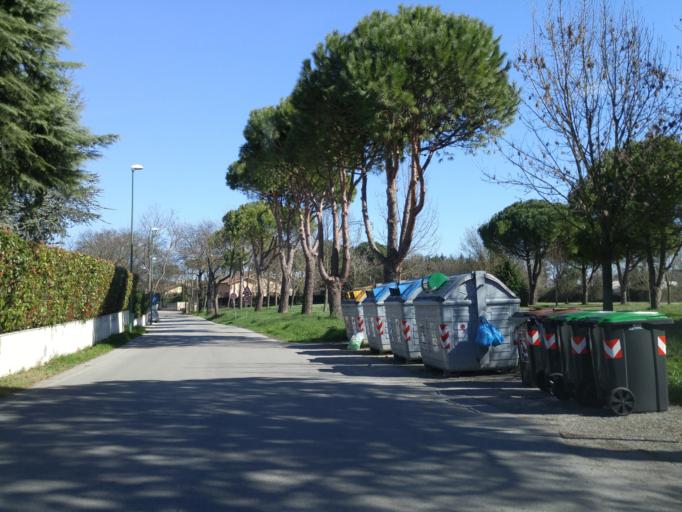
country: IT
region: Emilia-Romagna
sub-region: Provincia di Rimini
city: San Giovanni in Marignano
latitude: 43.9411
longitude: 12.7175
